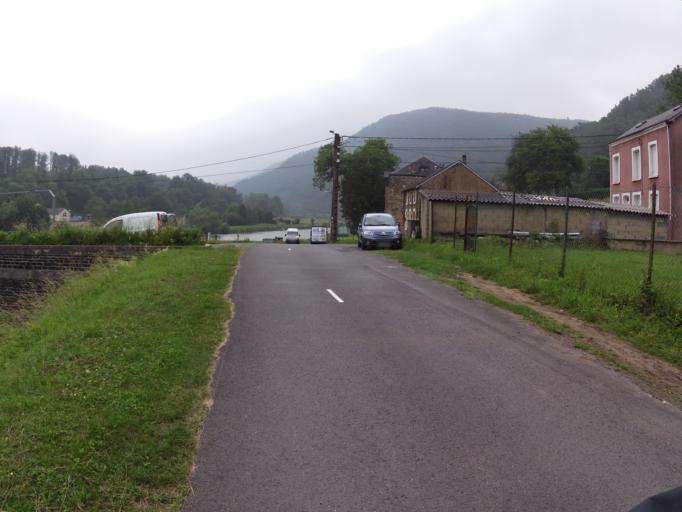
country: FR
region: Champagne-Ardenne
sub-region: Departement des Ardennes
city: Revin
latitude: 49.9437
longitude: 4.6446
